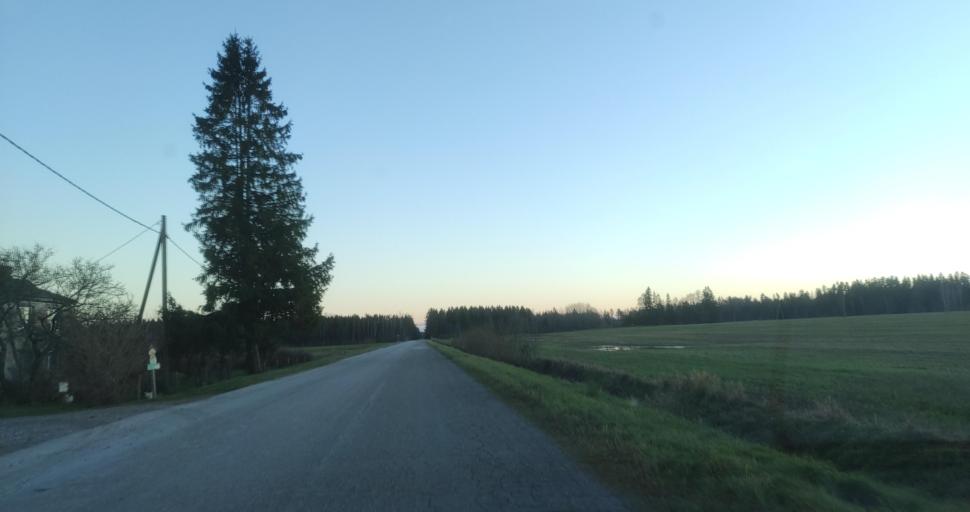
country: LV
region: Dundaga
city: Dundaga
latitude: 57.3731
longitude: 22.2317
